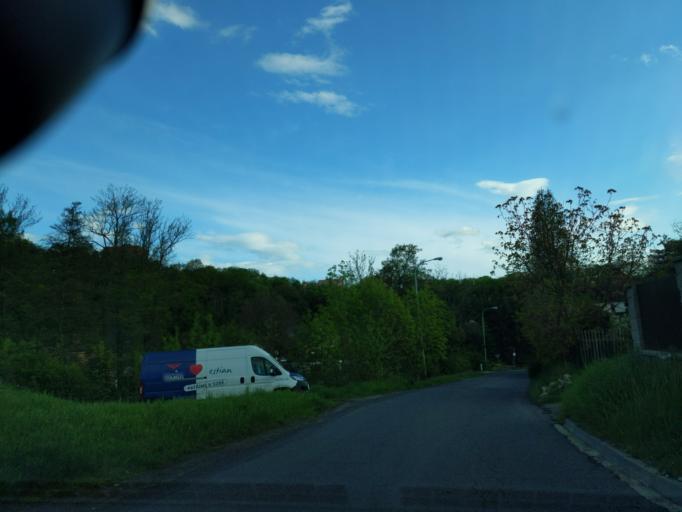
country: CZ
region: Ustecky
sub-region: Okres Usti nad Labem
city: Usti nad Labem
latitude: 50.6876
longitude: 14.0205
